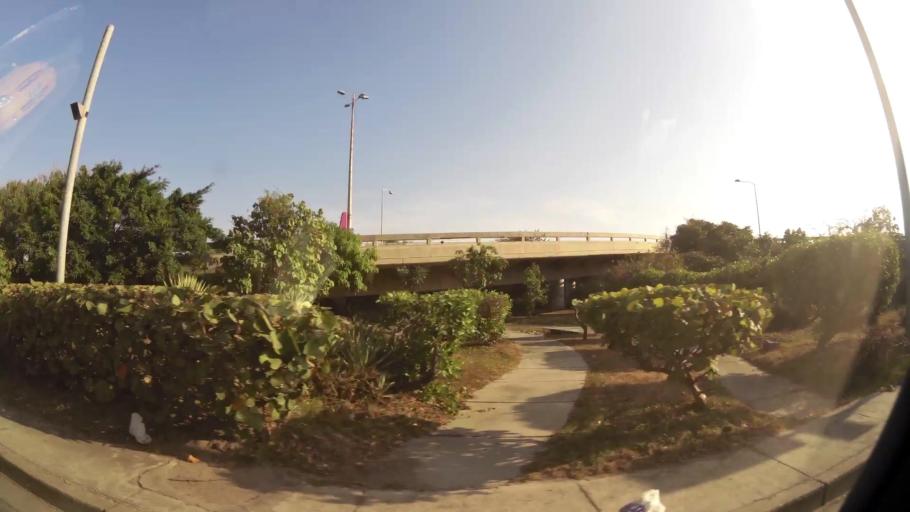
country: CO
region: Bolivar
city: Cartagena
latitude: 10.4427
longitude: -75.5257
